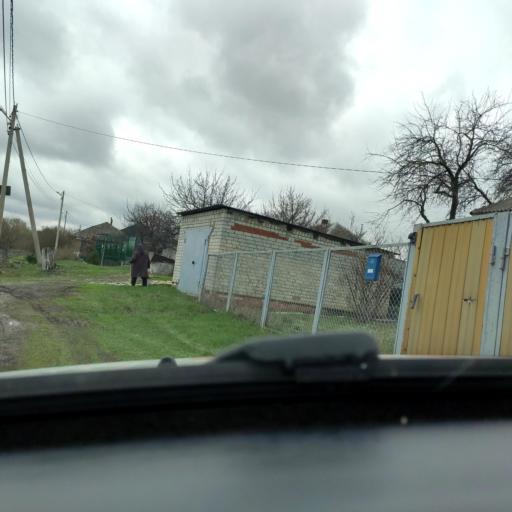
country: RU
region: Voronezj
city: Pridonskoy
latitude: 51.6484
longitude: 39.0641
